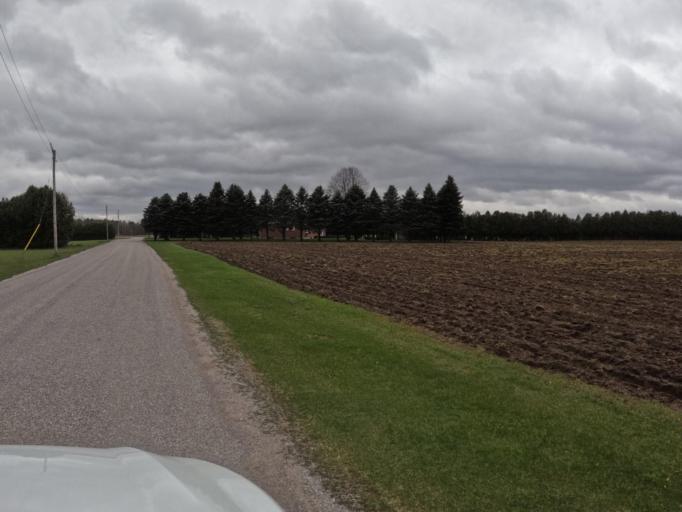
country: CA
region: Ontario
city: Norfolk County
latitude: 42.9703
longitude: -80.4269
